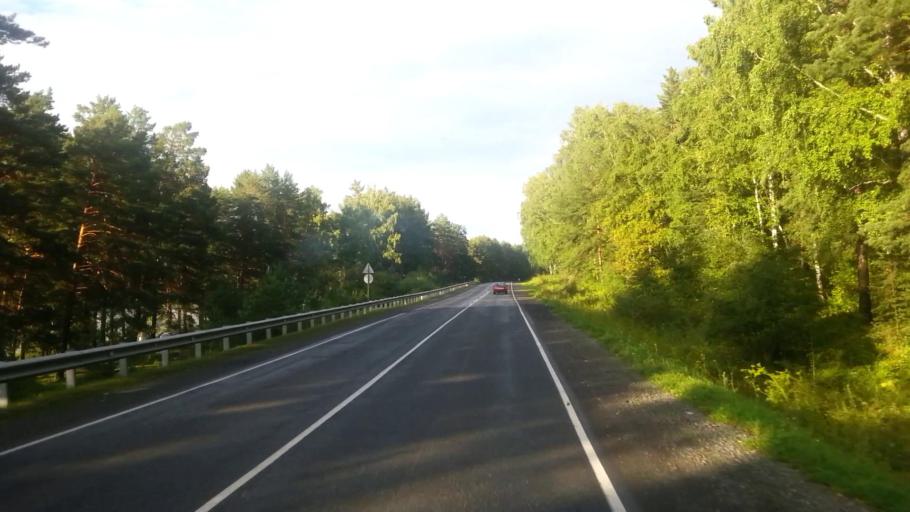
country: RU
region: Altay
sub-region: Mayminskiy Rayon
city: Manzherok
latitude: 51.8112
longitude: 85.7614
